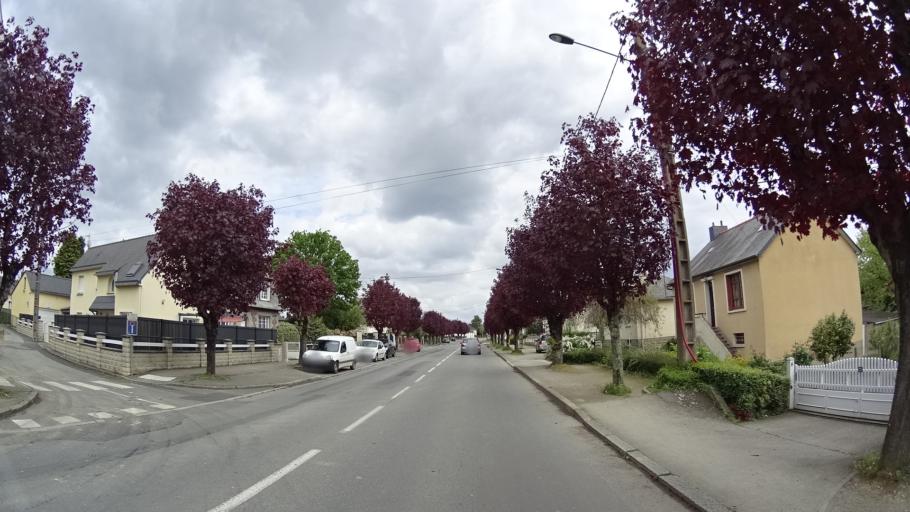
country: FR
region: Brittany
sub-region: Departement d'Ille-et-Vilaine
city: Mordelles
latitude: 48.0760
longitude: -1.8419
